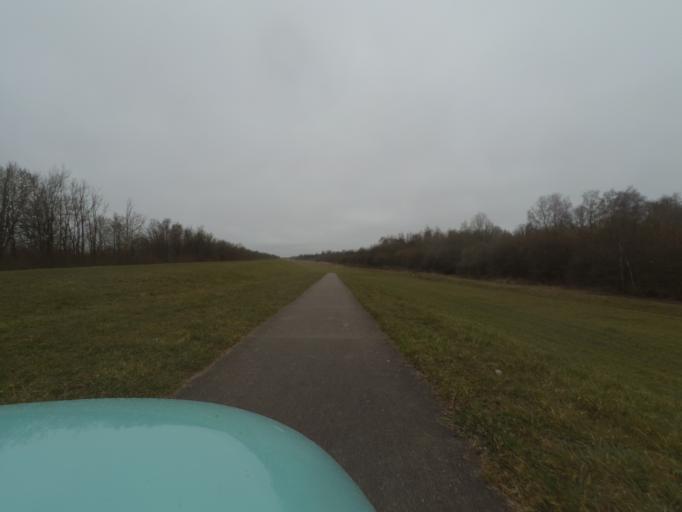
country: NL
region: Flevoland
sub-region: Gemeente Zeewolde
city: Zeewolde
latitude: 52.3028
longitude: 5.5408
